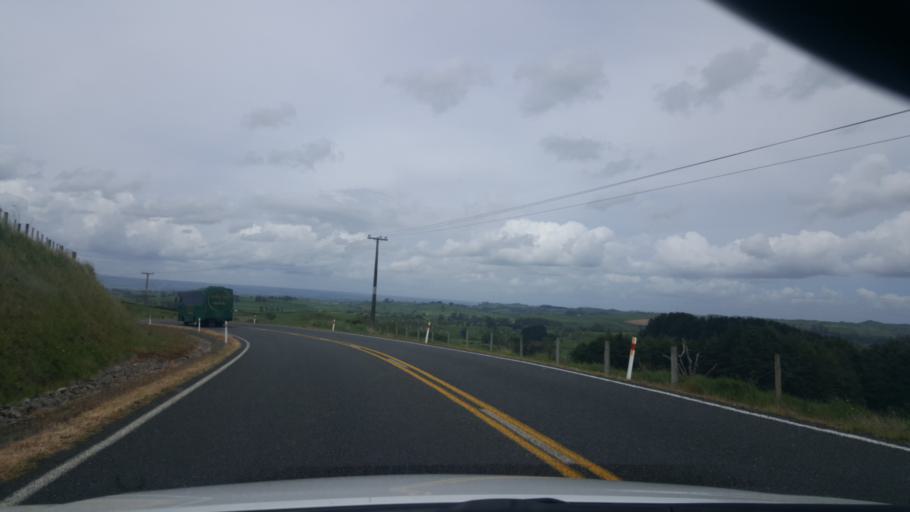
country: NZ
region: Waikato
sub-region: Matamata-Piako District
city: Matamata
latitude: -37.8788
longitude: 175.6893
